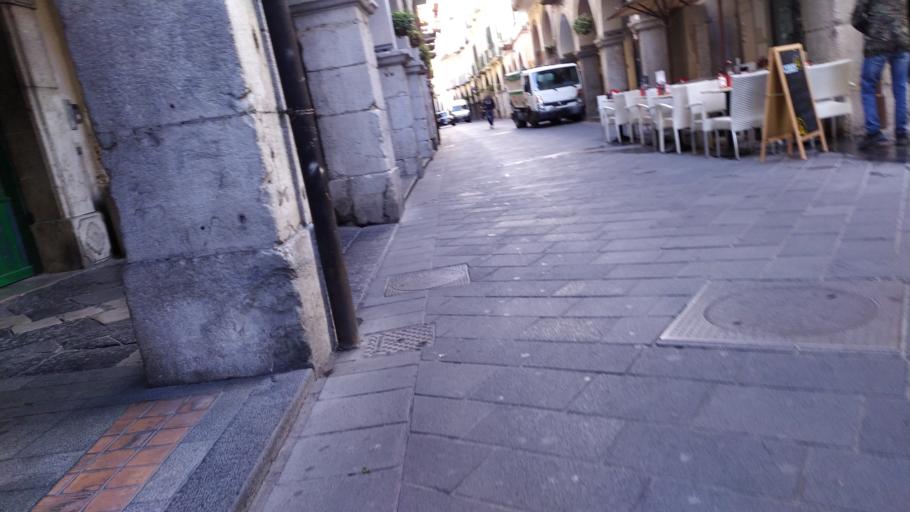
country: IT
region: Campania
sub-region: Provincia di Salerno
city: Cava De Tirreni
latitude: 40.6989
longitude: 14.7088
